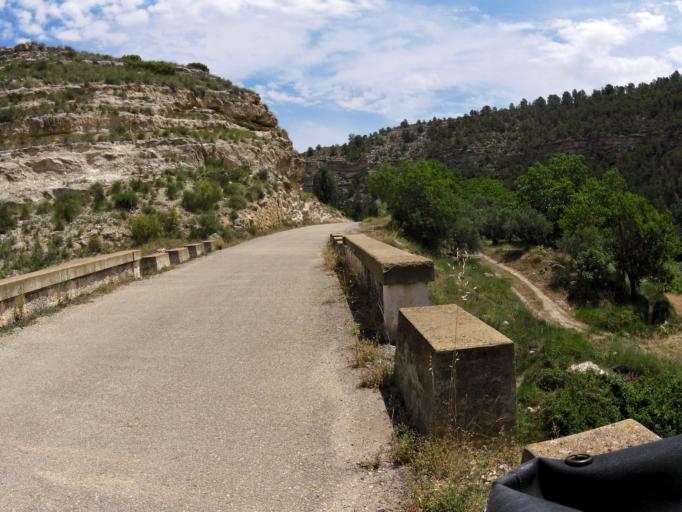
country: ES
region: Castille-La Mancha
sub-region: Provincia de Albacete
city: Casas de Juan Nunez
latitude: 39.1592
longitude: -1.6021
